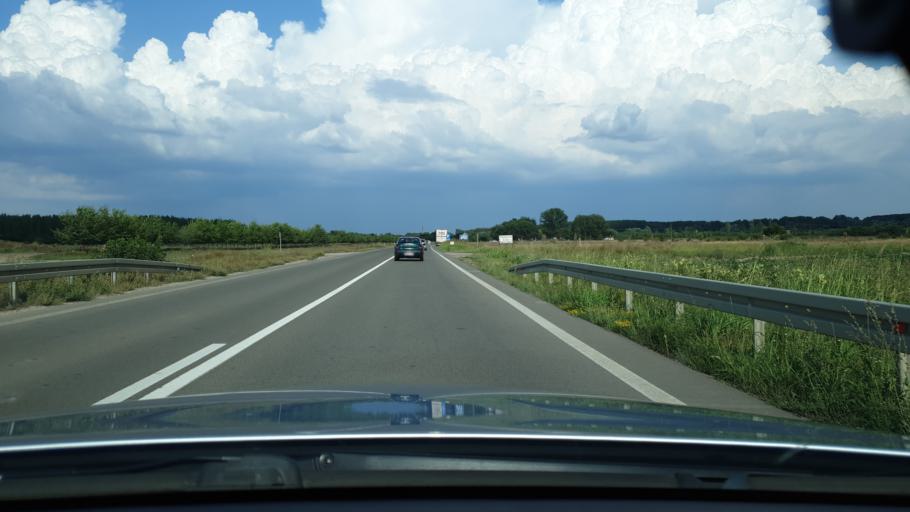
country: RS
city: Taras
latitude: 45.3987
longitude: 20.1933
